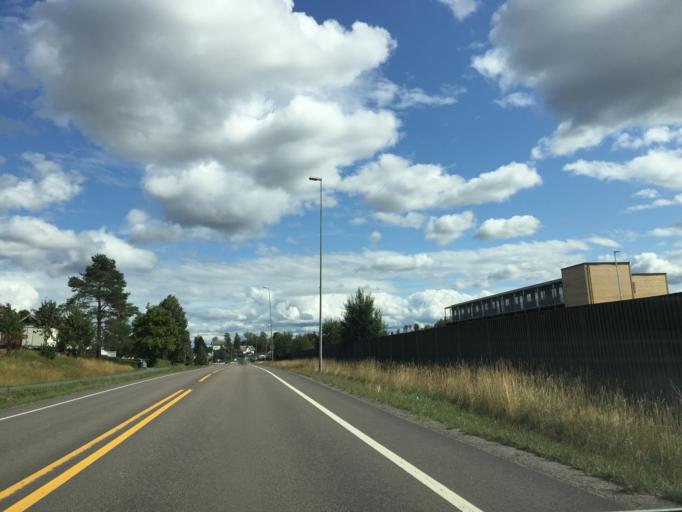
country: NO
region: Ostfold
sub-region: Spydeberg
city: Spydeberg
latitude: 59.6167
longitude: 11.0595
